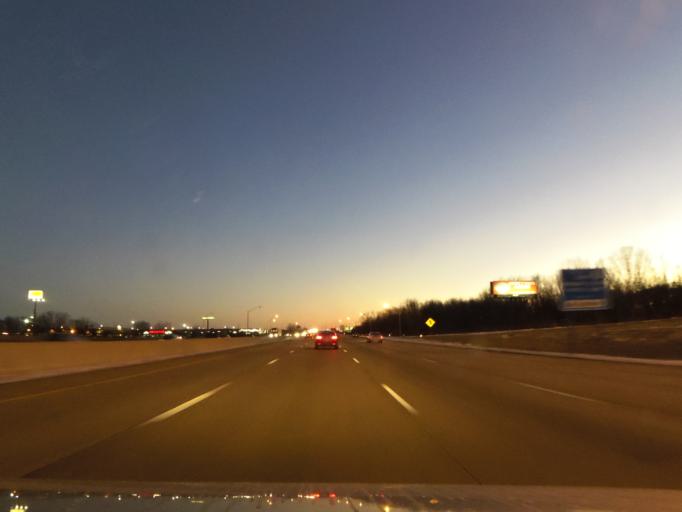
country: US
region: Indiana
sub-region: Lake County
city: Merrillville
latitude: 41.5068
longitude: -87.3200
